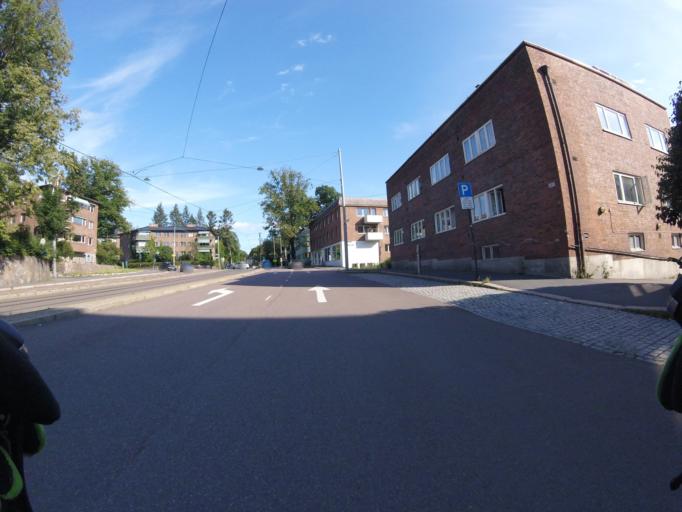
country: NO
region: Oslo
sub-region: Oslo
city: Sjolyststranda
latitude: 59.9202
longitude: 10.6909
